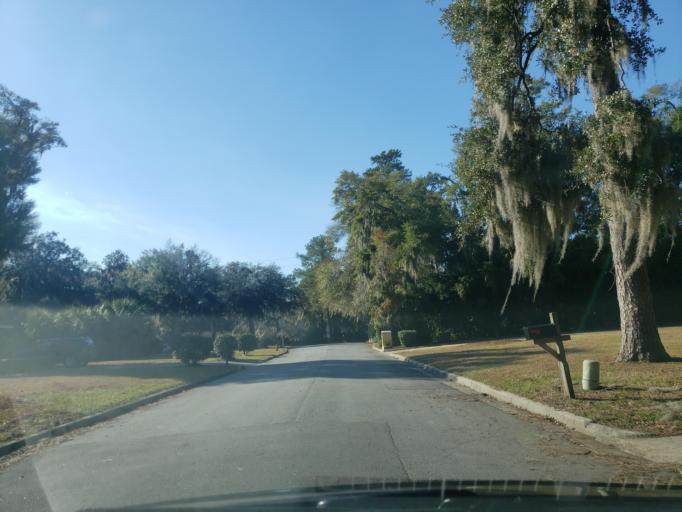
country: US
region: Georgia
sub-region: Chatham County
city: Whitemarsh Island
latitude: 32.0578
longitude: -81.0176
